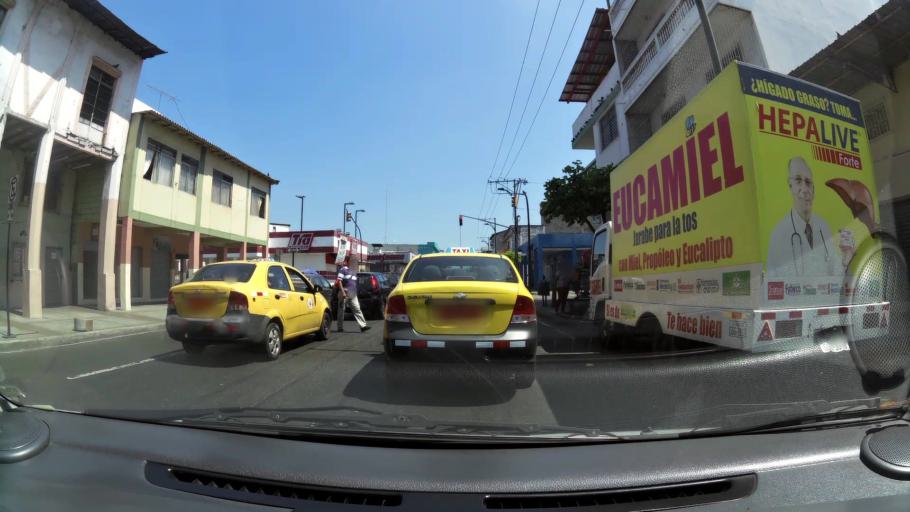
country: EC
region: Guayas
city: Guayaquil
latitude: -2.2037
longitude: -79.9088
